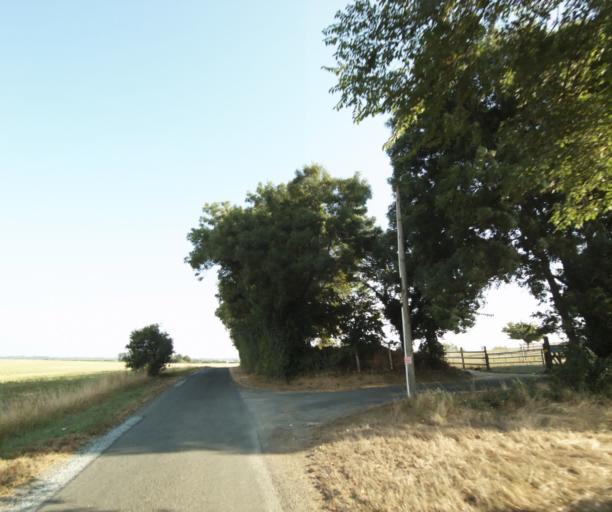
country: FR
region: Poitou-Charentes
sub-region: Departement de la Charente-Maritime
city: Muron
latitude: 45.9762
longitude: -0.8268
